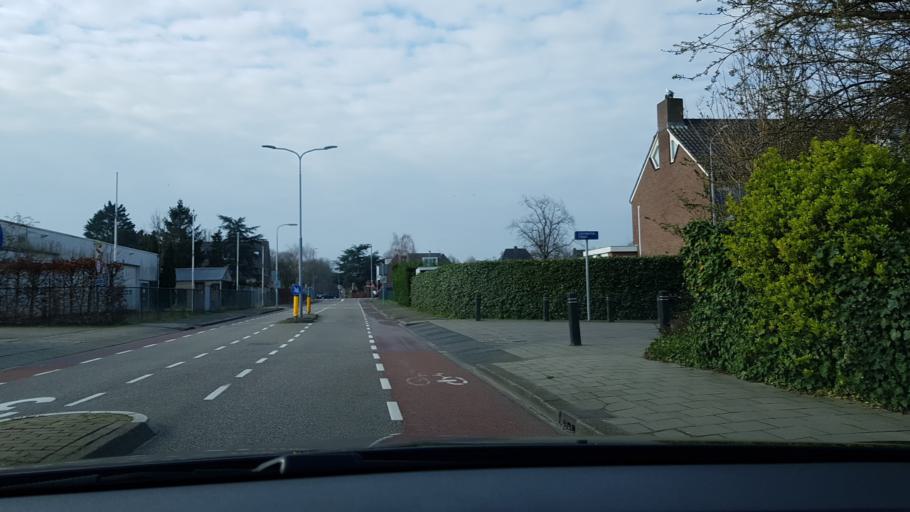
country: NL
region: North Holland
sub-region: Gemeente Haarlemmermeer
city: Hoofddorp
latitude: 52.3013
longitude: 4.7041
